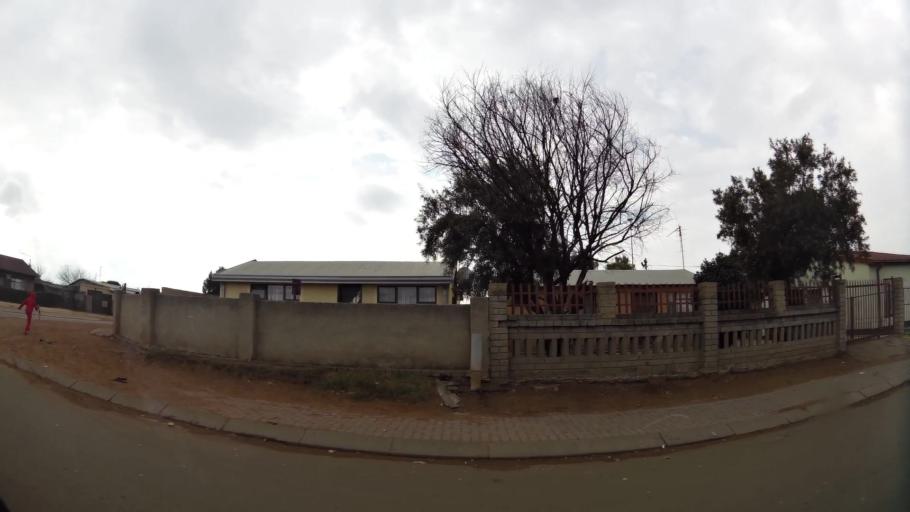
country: ZA
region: Gauteng
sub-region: Sedibeng District Municipality
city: Vanderbijlpark
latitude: -26.6648
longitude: 27.8508
